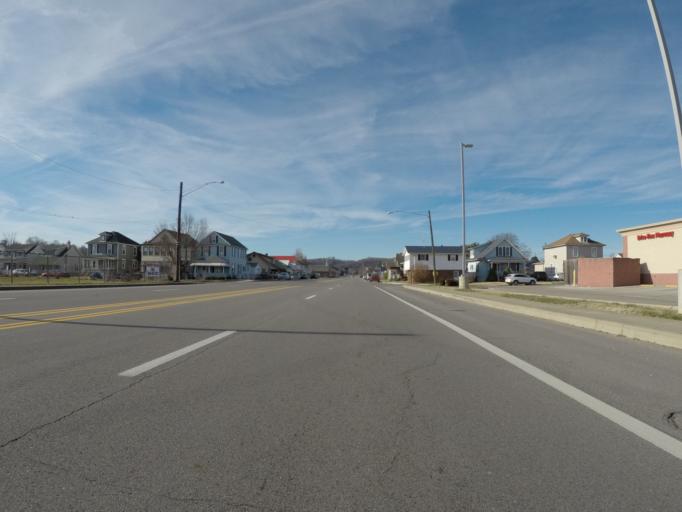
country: US
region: West Virginia
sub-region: Wayne County
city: Kenova
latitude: 38.4012
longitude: -82.5777
